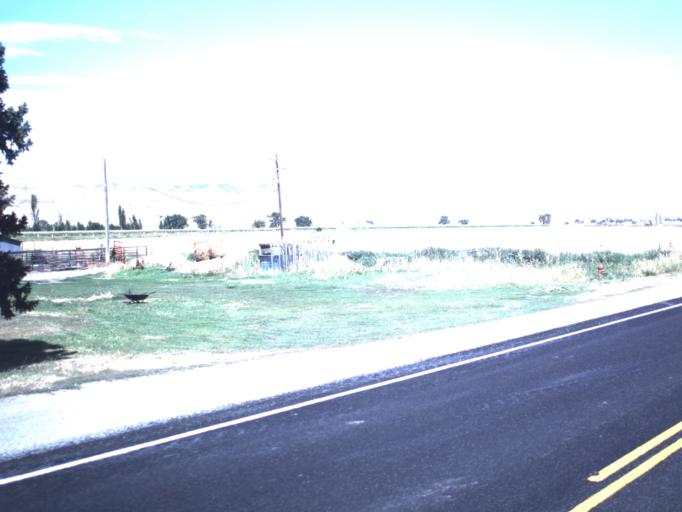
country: US
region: Utah
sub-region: Box Elder County
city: Garland
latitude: 41.7699
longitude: -112.1489
